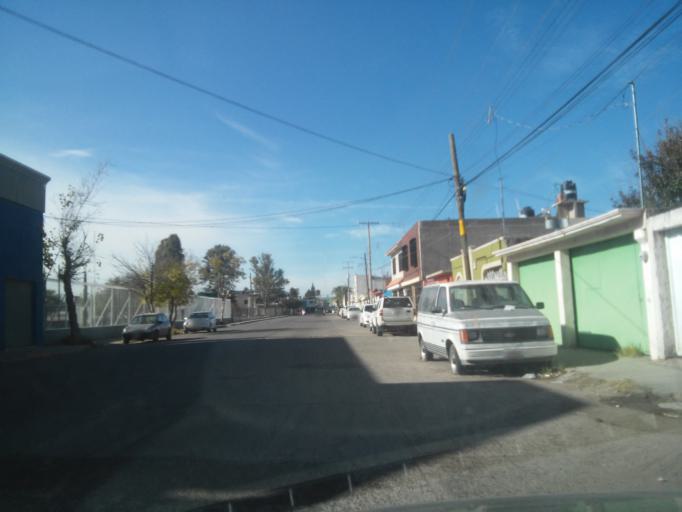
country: MX
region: Durango
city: Victoria de Durango
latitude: 24.0423
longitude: -104.6551
